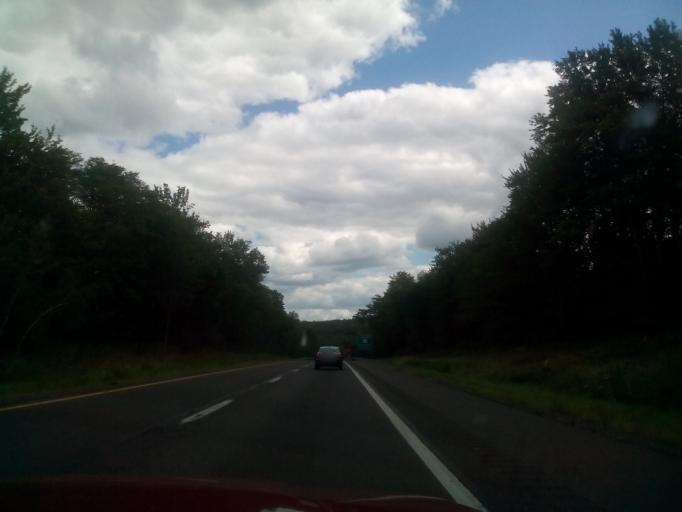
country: US
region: Pennsylvania
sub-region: Carbon County
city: Towamensing Trails
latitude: 41.0814
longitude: -75.6192
